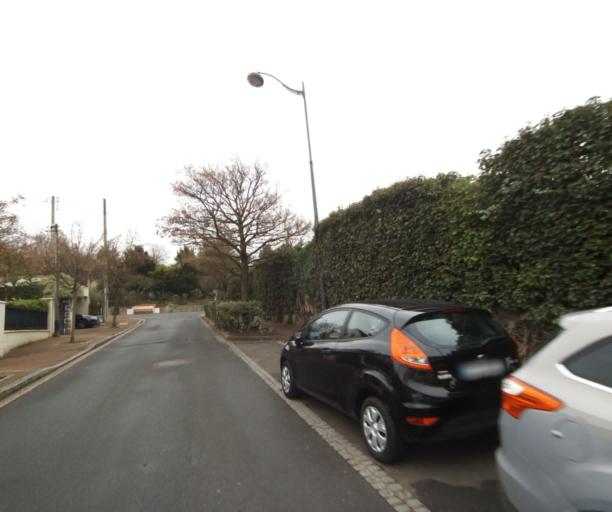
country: FR
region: Ile-de-France
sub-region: Departement des Hauts-de-Seine
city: Rueil-Malmaison
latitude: 48.8806
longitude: 2.1929
